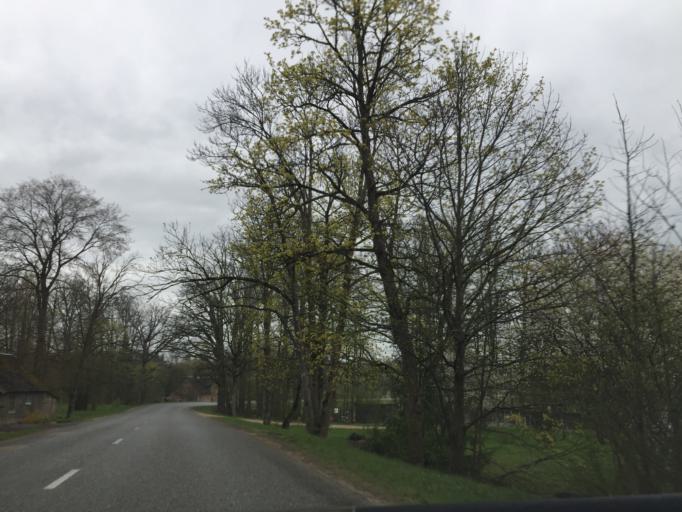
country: LV
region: Sigulda
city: Sigulda
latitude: 57.0275
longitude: 24.8168
